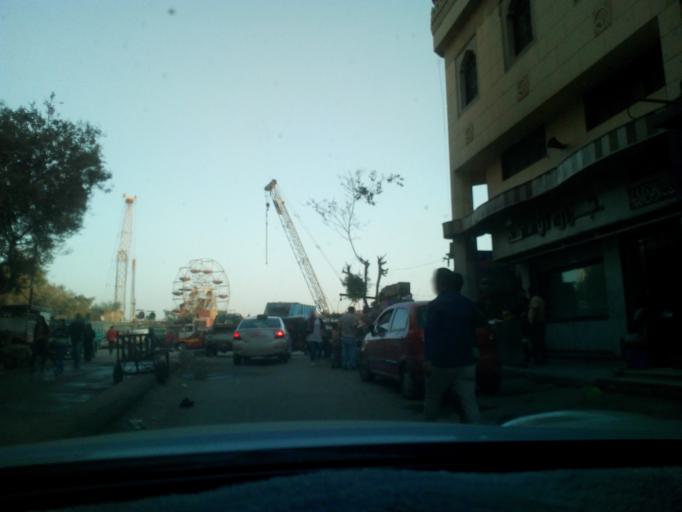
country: EG
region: Muhafazat al Qalyubiyah
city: Al Khankah
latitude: 30.1271
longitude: 31.3512
